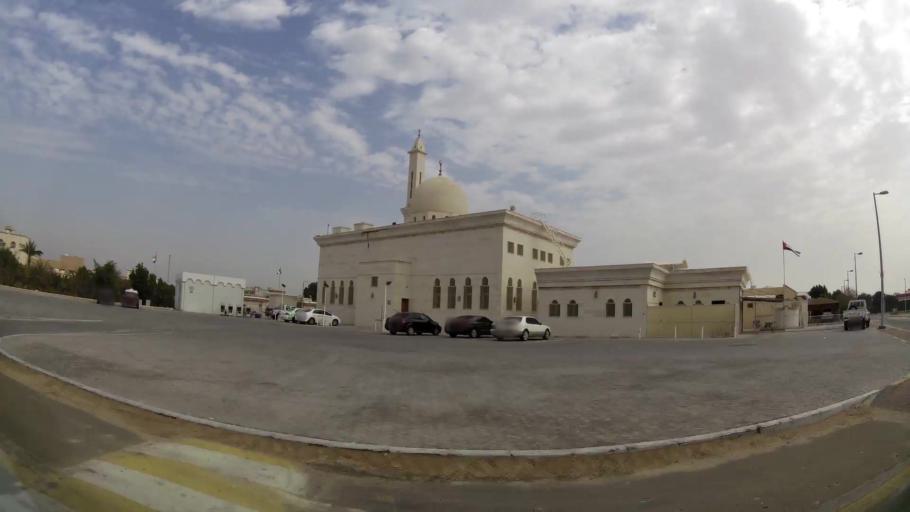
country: AE
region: Abu Dhabi
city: Abu Dhabi
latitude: 24.3129
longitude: 54.6402
